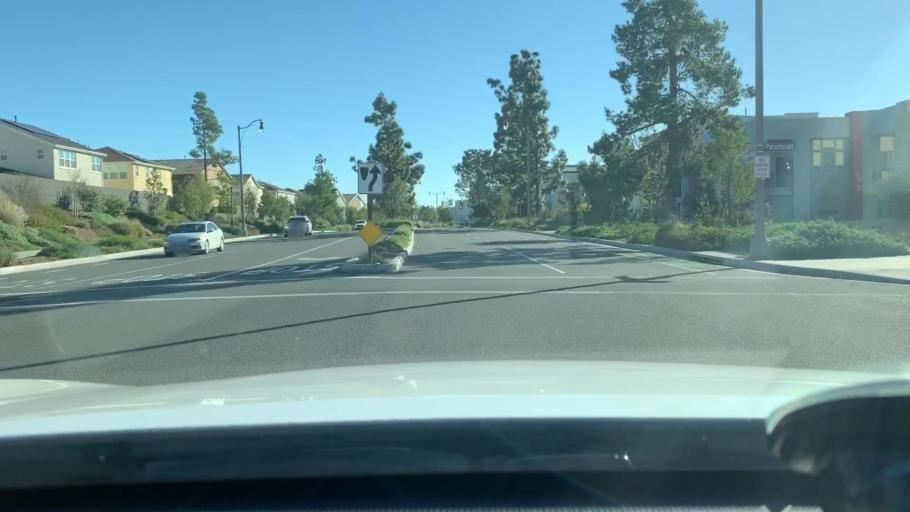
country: US
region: California
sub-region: Orange County
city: Lake Forest
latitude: 33.6877
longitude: -117.7389
